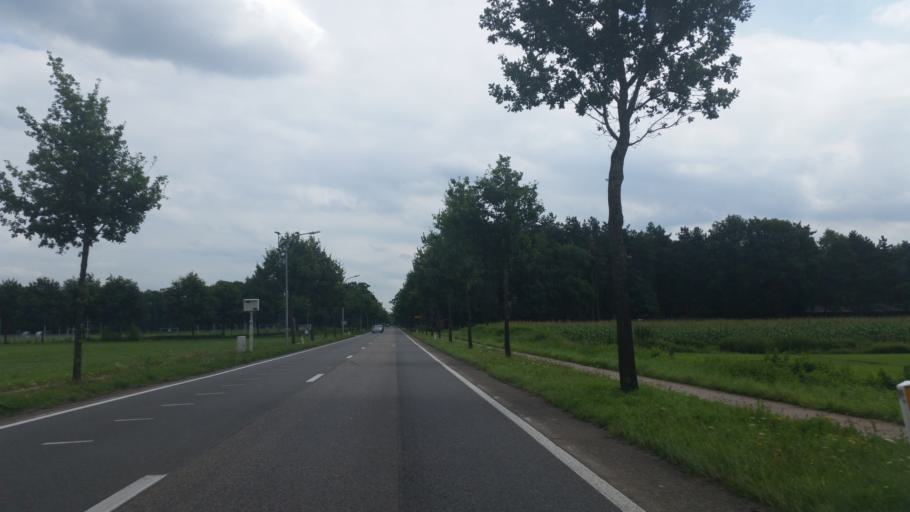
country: BE
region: Flanders
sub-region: Provincie Antwerpen
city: Vosselaar
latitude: 51.3416
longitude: 4.8979
